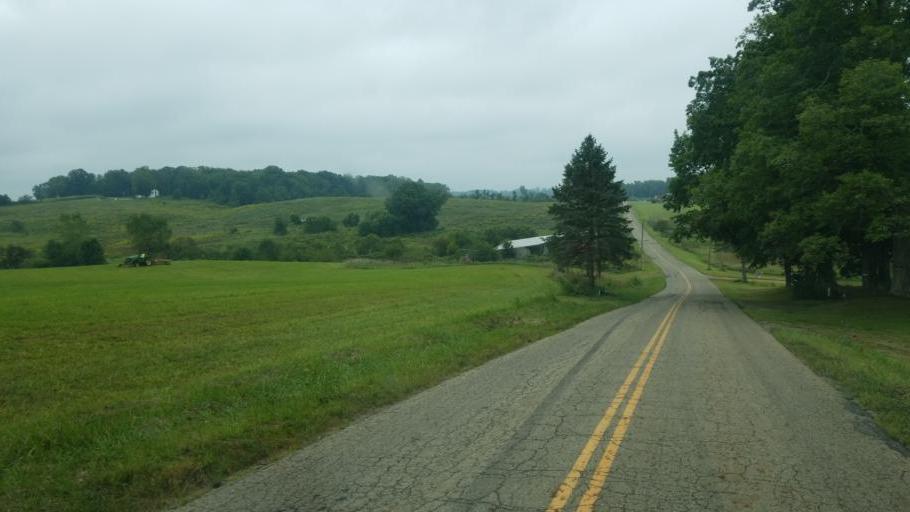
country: US
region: Ohio
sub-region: Licking County
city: Utica
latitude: 40.2667
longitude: -82.4154
